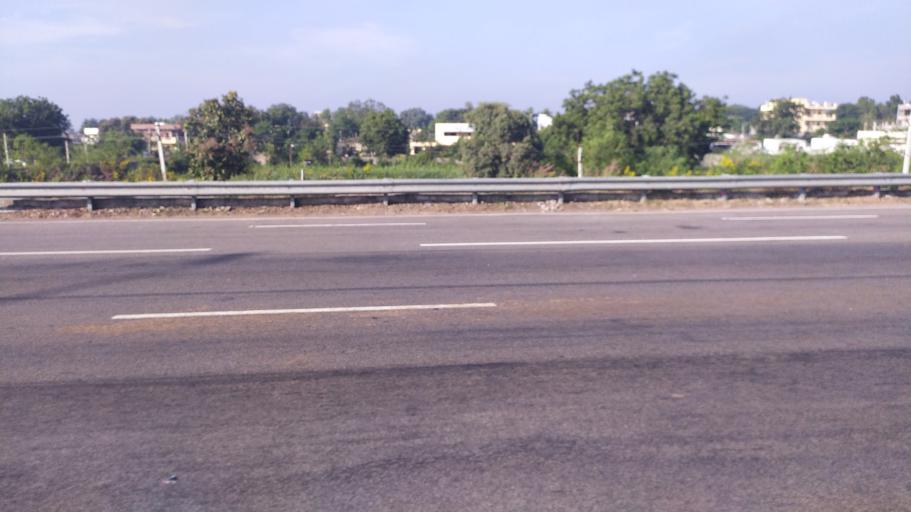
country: IN
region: Telangana
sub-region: Hyderabad
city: Hyderabad
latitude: 17.3399
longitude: 78.3656
